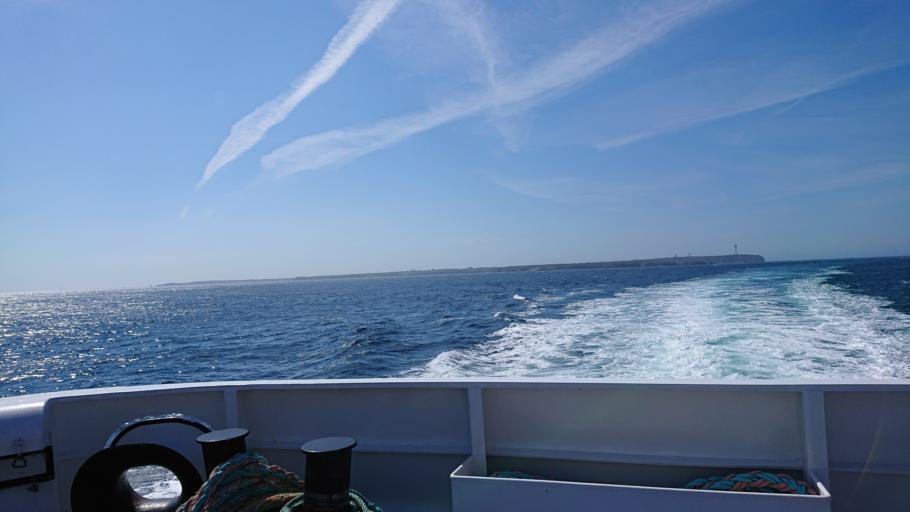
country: FR
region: Brittany
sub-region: Departement du Finistere
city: Porspoder
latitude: 48.4484
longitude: -5.0029
